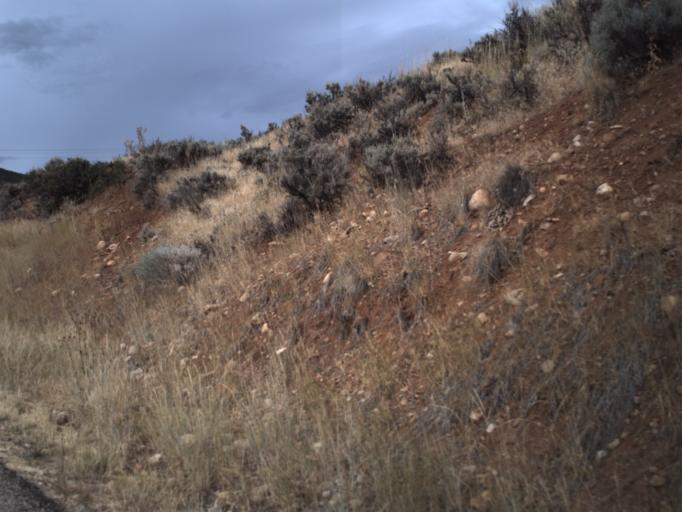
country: US
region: Utah
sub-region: Morgan County
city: Morgan
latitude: 40.9226
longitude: -111.5964
